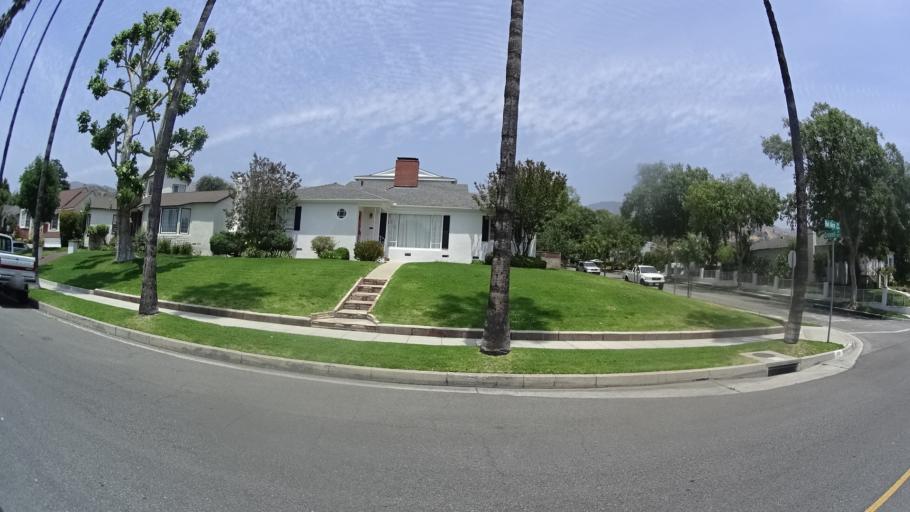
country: US
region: California
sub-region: Los Angeles County
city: Burbank
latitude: 34.1954
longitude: -118.3061
